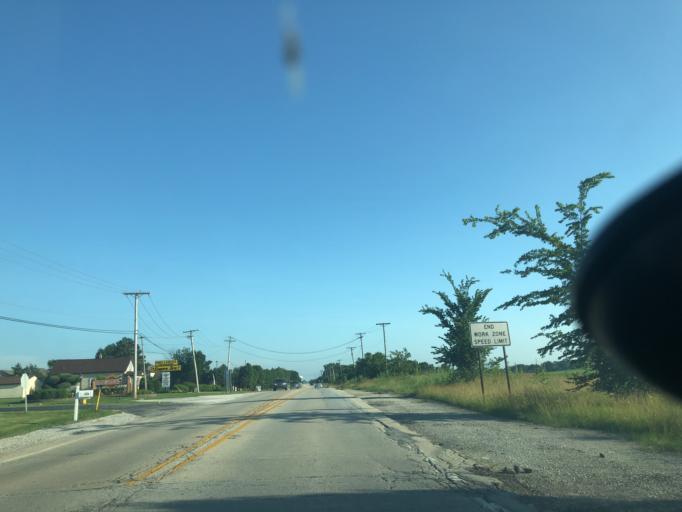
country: US
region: Illinois
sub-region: Will County
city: Homer Glen
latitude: 41.5959
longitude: -87.8913
